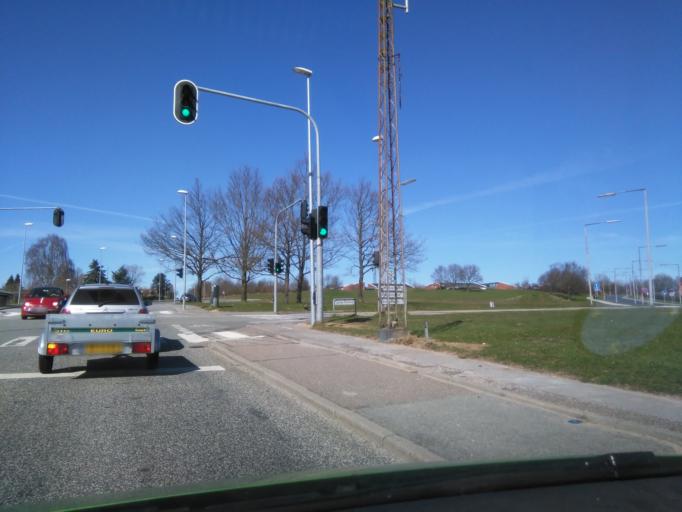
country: DK
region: Central Jutland
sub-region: Arhus Kommune
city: Lystrup
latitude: 56.2340
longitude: 10.2302
